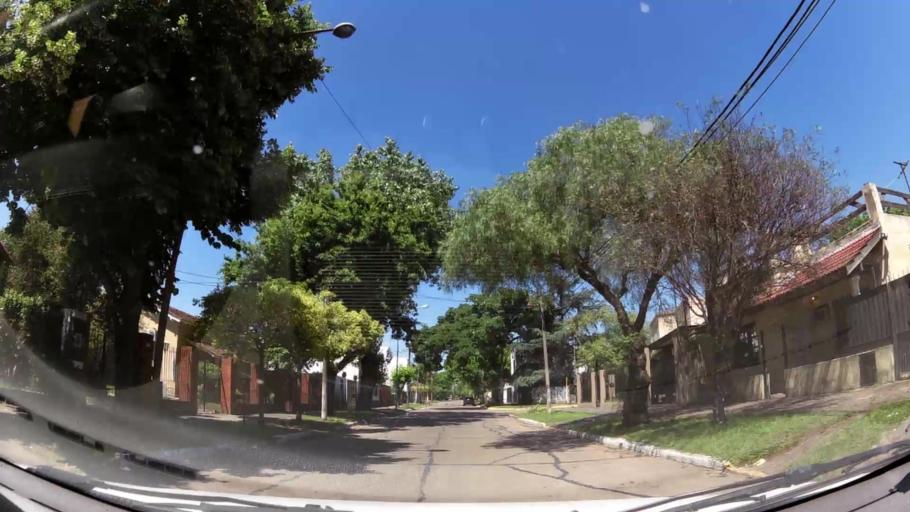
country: AR
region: Buenos Aires
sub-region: Partido de Merlo
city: Merlo
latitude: -34.6756
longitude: -58.6891
